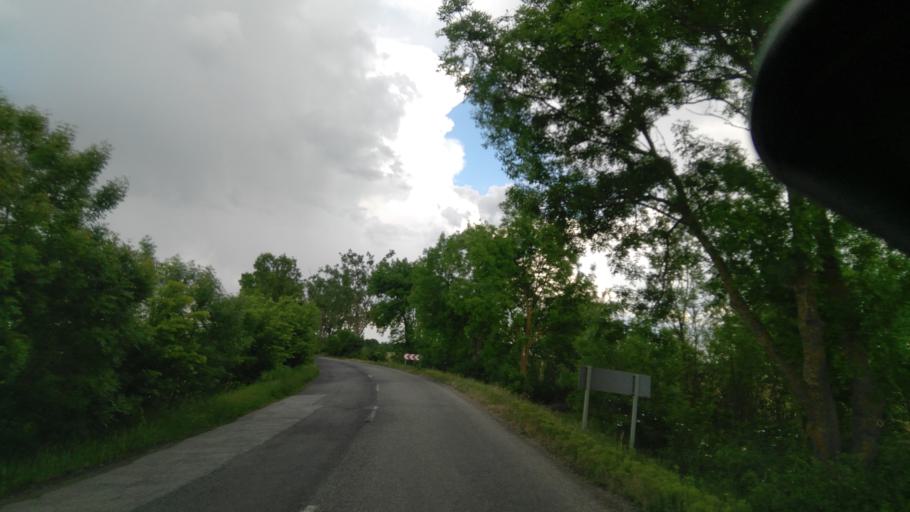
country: HU
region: Bekes
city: Fuzesgyarmat
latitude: 47.1501
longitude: 21.1273
